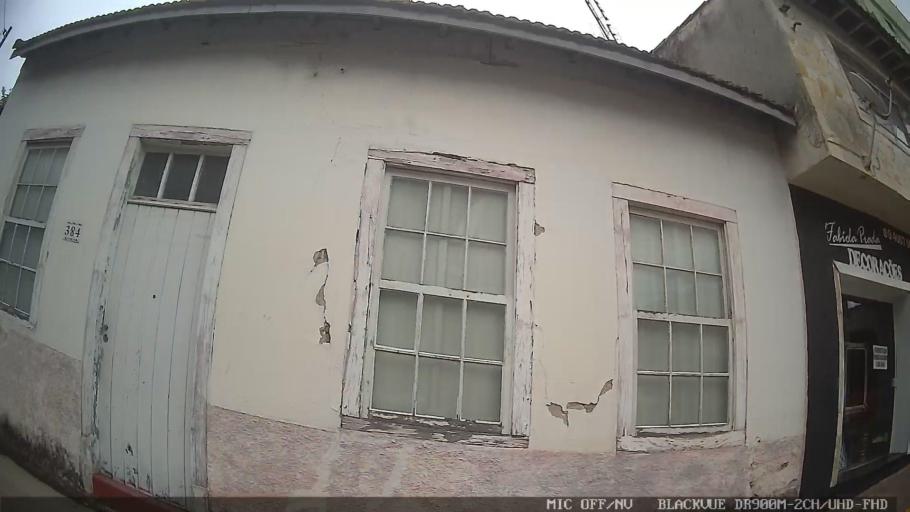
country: BR
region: Sao Paulo
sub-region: Atibaia
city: Atibaia
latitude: -23.1177
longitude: -46.5508
